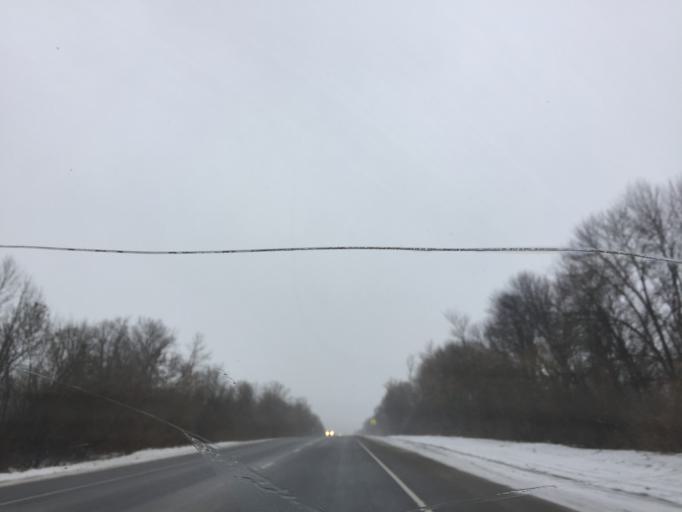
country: RU
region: Tula
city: Plavsk
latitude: 53.7356
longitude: 37.3121
